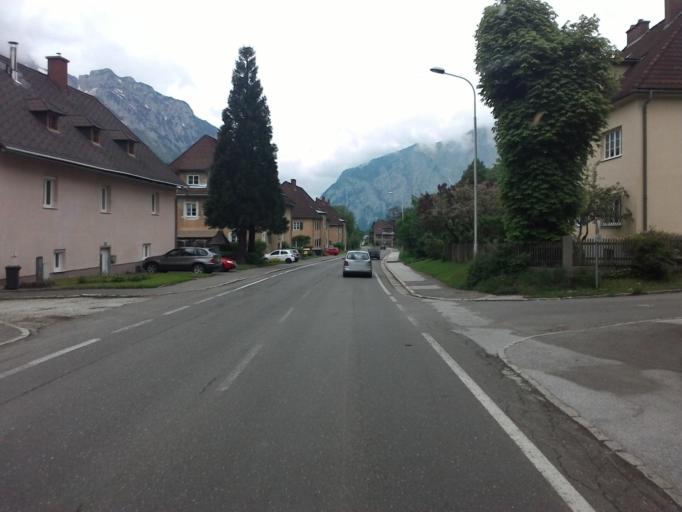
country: AT
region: Styria
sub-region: Politischer Bezirk Leoben
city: Eisenerz
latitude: 47.5446
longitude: 14.8840
